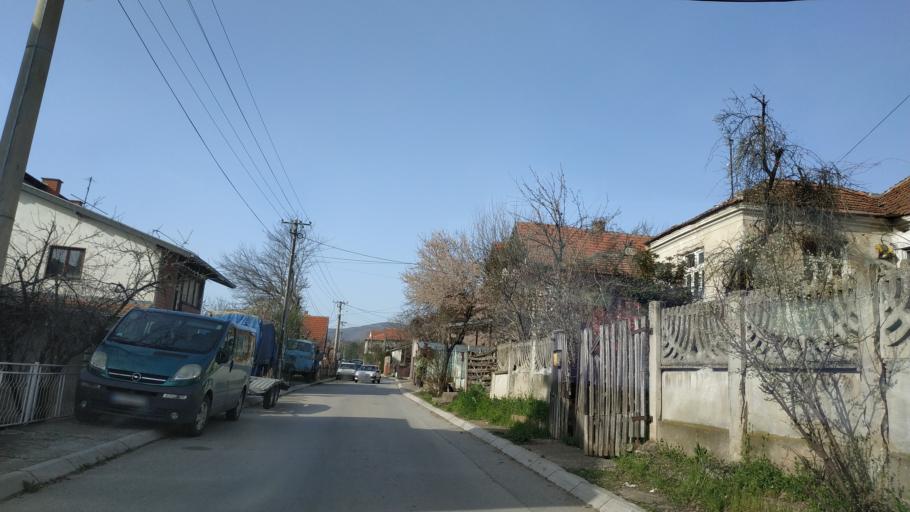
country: RS
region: Central Serbia
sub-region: Nisavski Okrug
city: Aleksinac
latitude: 43.5430
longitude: 21.7169
